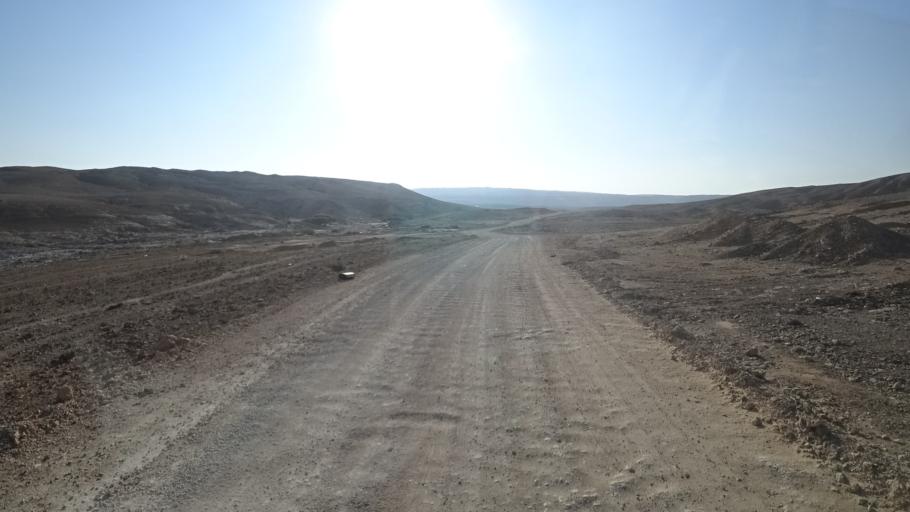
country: OM
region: Zufar
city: Salalah
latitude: 17.2422
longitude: 53.9125
